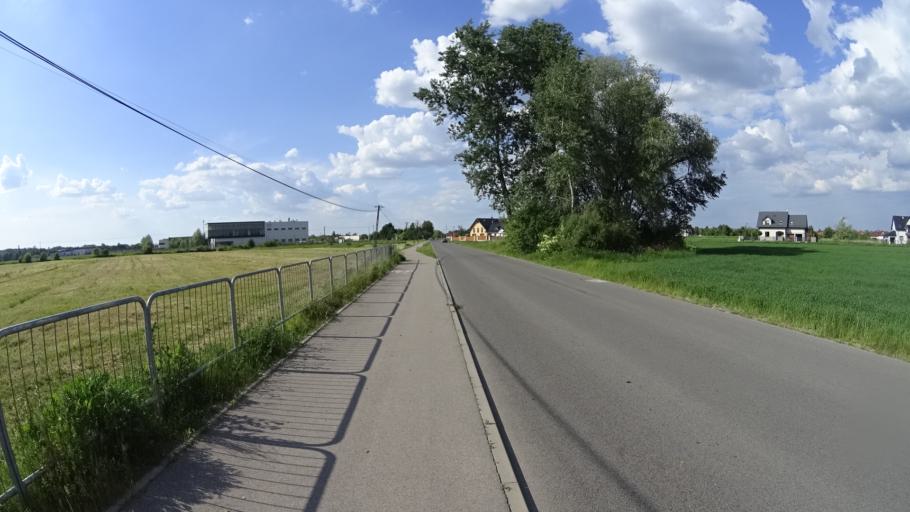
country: PL
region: Masovian Voivodeship
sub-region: Powiat pruszkowski
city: Nadarzyn
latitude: 52.0803
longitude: 20.8172
